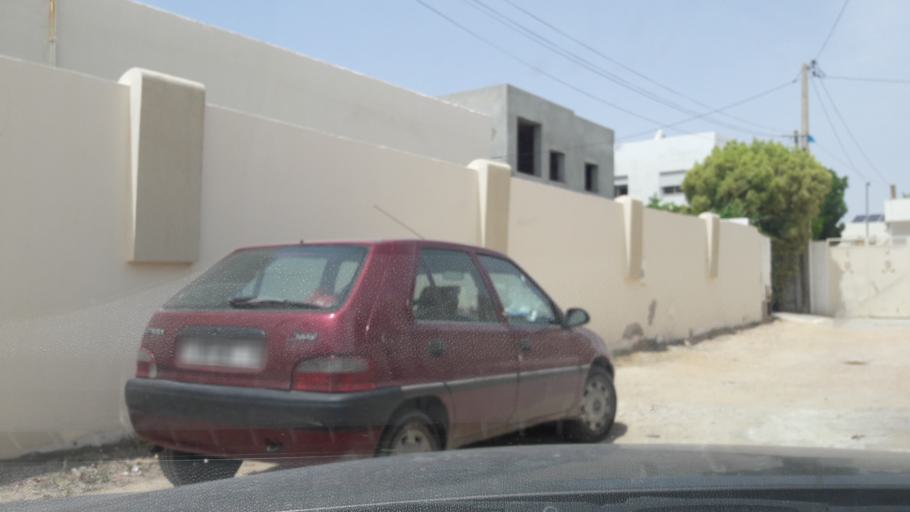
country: TN
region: Safaqis
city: Al Qarmadah
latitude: 34.7846
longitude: 10.7591
